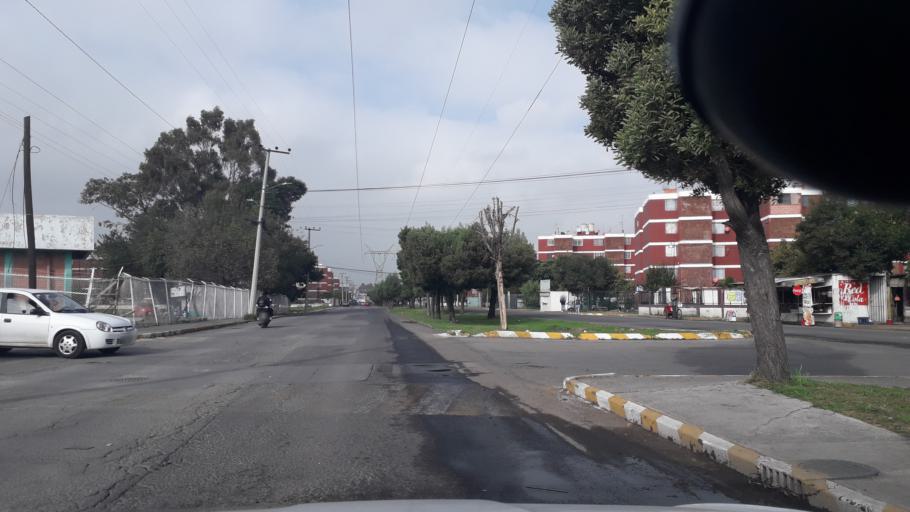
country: MX
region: Mexico
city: Coacalco
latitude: 19.6446
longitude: -99.0831
